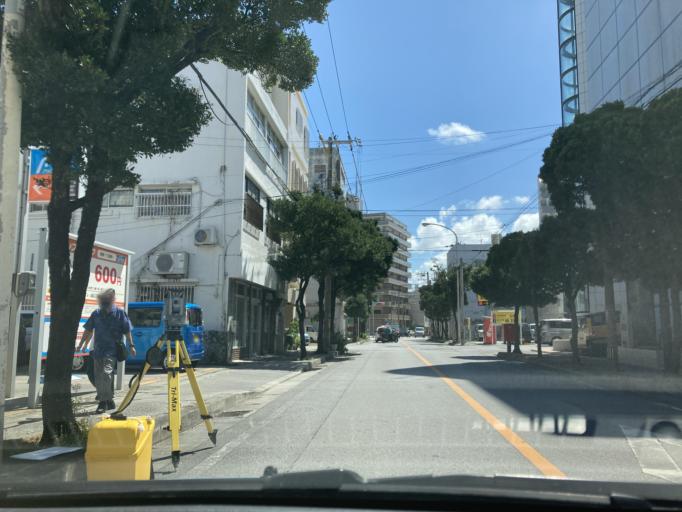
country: JP
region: Okinawa
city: Naha-shi
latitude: 26.2186
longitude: 127.6725
